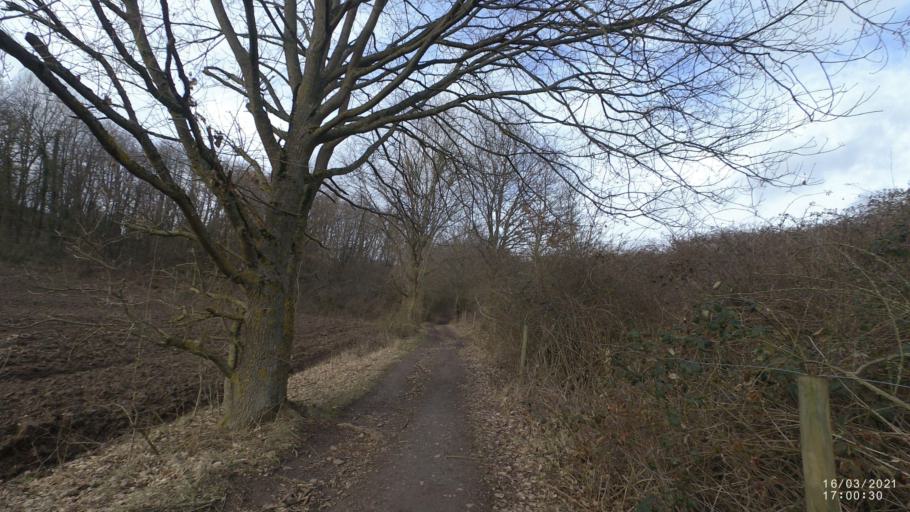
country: DE
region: Rheinland-Pfalz
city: Mendig
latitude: 50.3947
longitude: 7.2710
